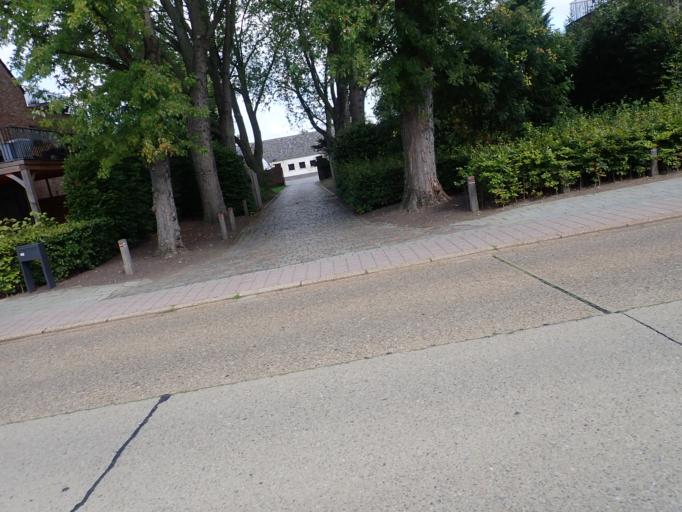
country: BE
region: Flanders
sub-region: Provincie Antwerpen
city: Herenthout
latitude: 51.1408
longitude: 4.7496
